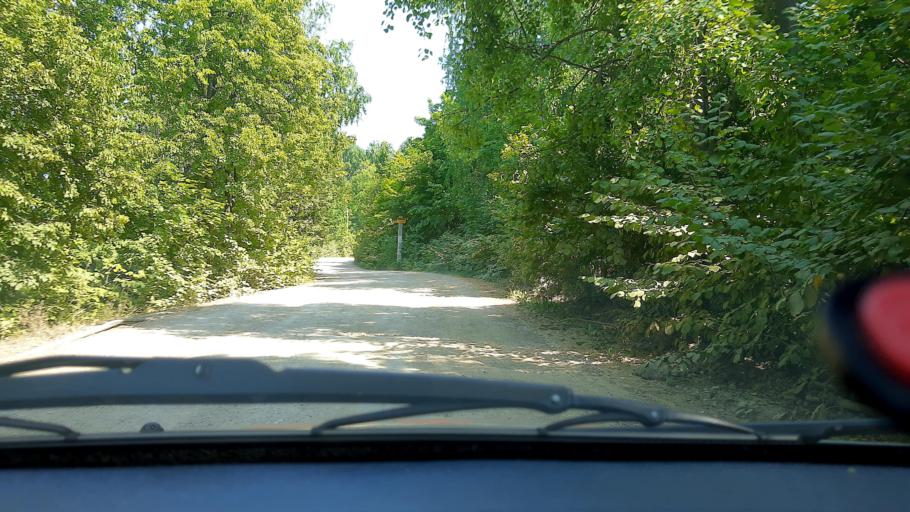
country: RU
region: Bashkortostan
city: Karmaskaly
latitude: 54.3869
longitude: 55.9067
